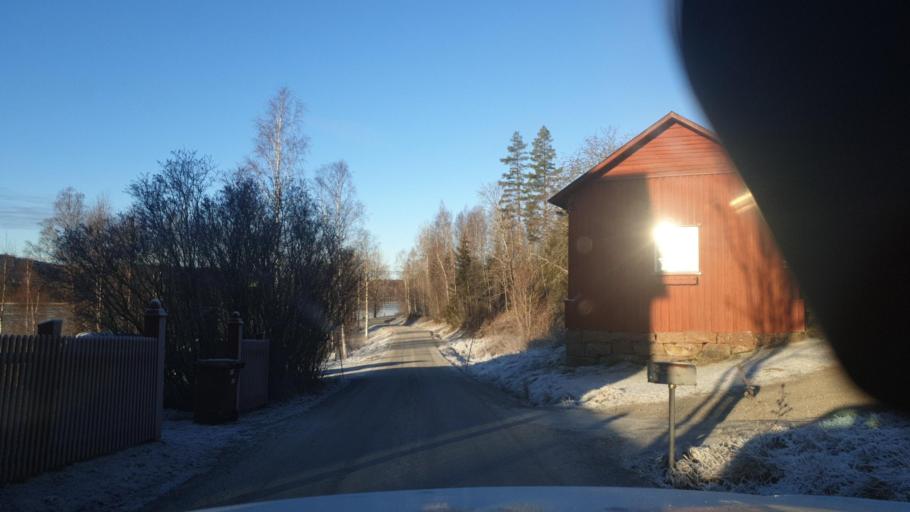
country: SE
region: Vaermland
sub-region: Arvika Kommun
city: Arvika
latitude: 59.7340
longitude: 12.8324
